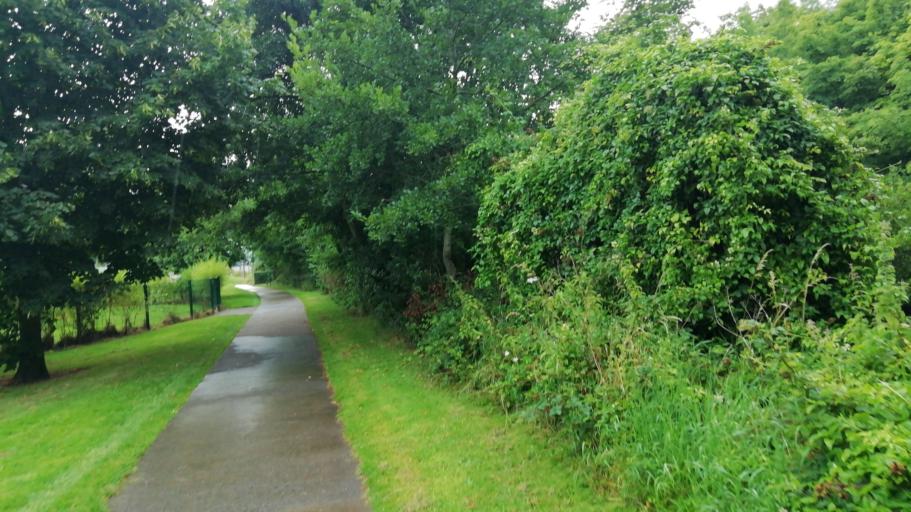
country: IE
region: Munster
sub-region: South Tipperary
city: Cluain Meala
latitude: 52.3512
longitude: -7.6987
